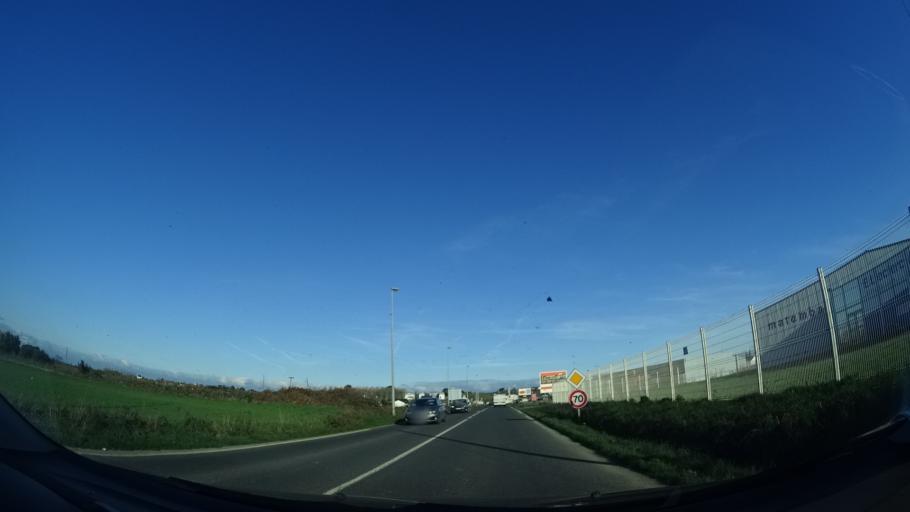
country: FR
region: Brittany
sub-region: Departement du Finistere
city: Saint-Pol-de-Leon
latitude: 48.6784
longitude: -4.0054
